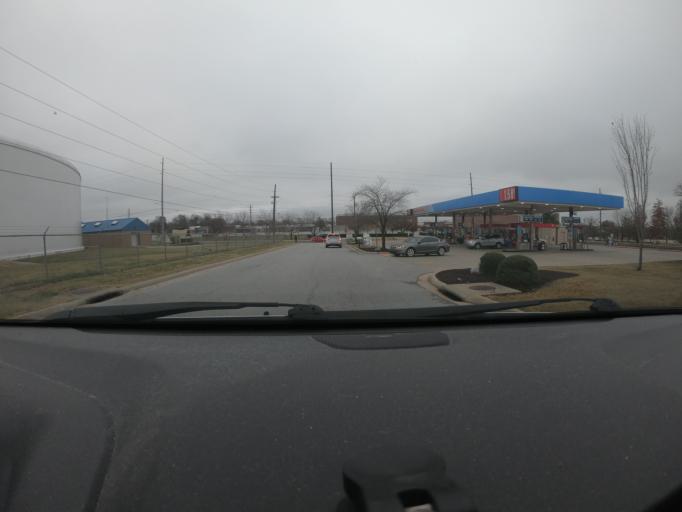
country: US
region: Arkansas
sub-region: Benton County
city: Bentonville
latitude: 36.3668
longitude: -94.2229
